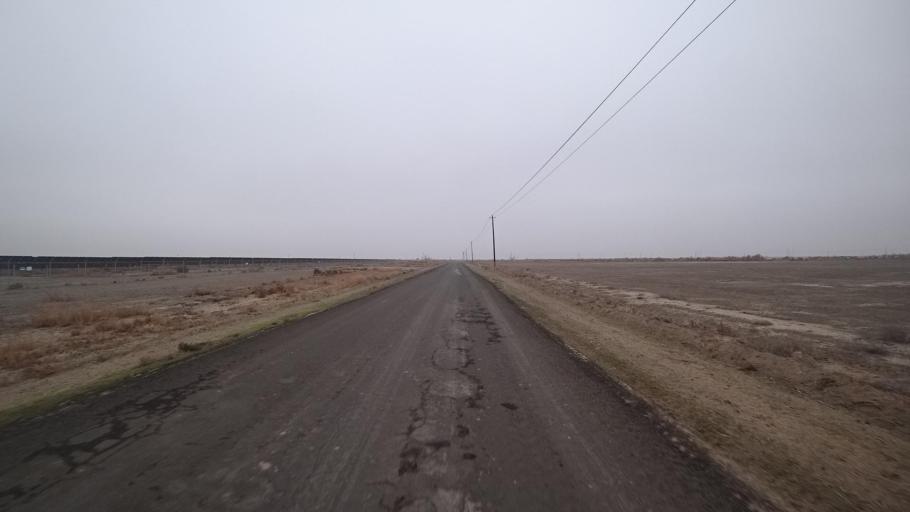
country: US
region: California
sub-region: Kern County
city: Lost Hills
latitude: 35.5911
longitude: -119.5806
